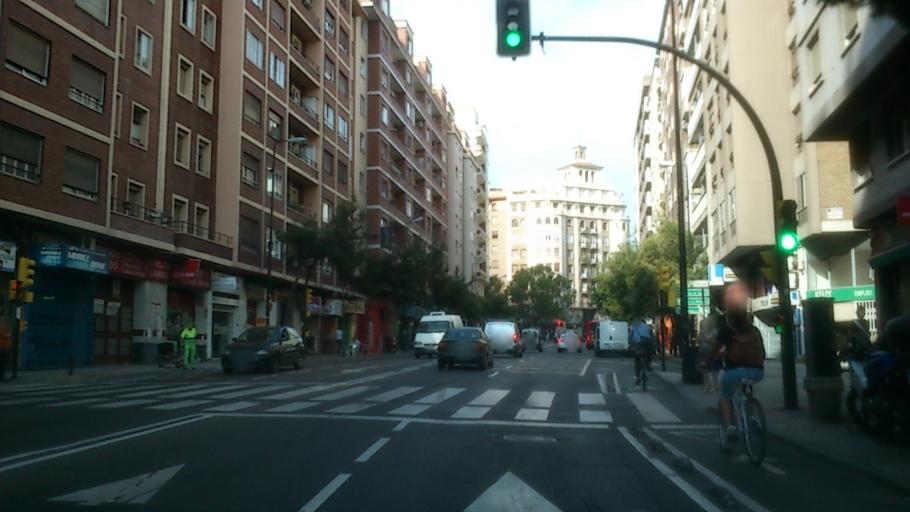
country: ES
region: Aragon
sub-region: Provincia de Zaragoza
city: Zaragoza
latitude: 41.6405
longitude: -0.8848
